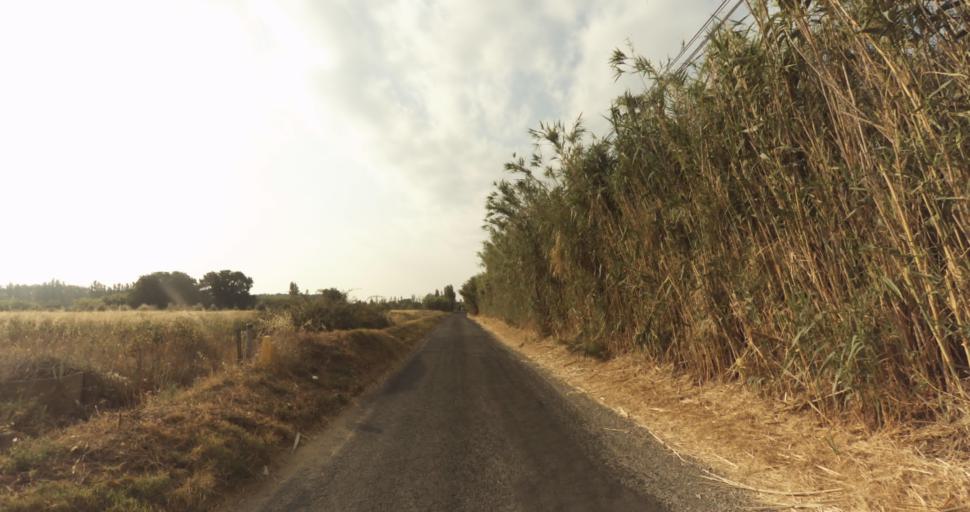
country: FR
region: Languedoc-Roussillon
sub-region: Departement des Pyrenees-Orientales
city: Theza
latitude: 42.6337
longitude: 2.9452
